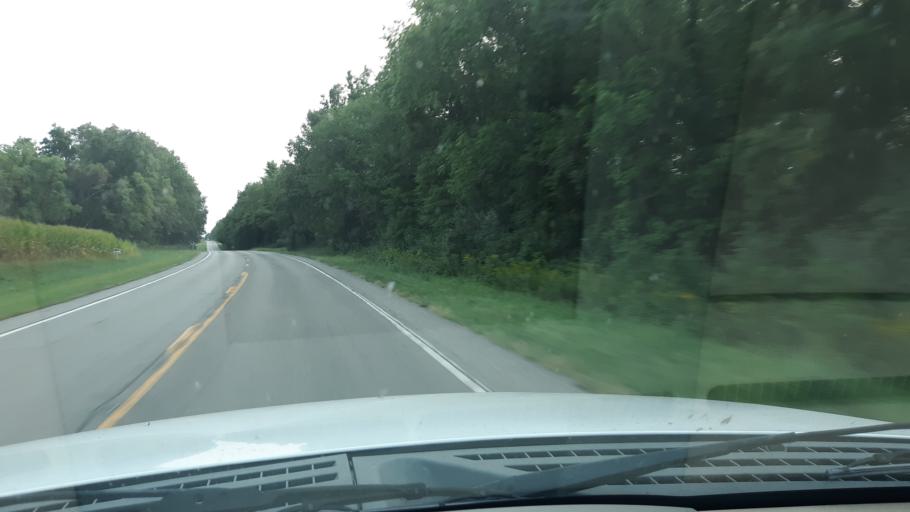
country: US
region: Illinois
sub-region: White County
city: Norris City
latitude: 37.9619
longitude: -88.3342
